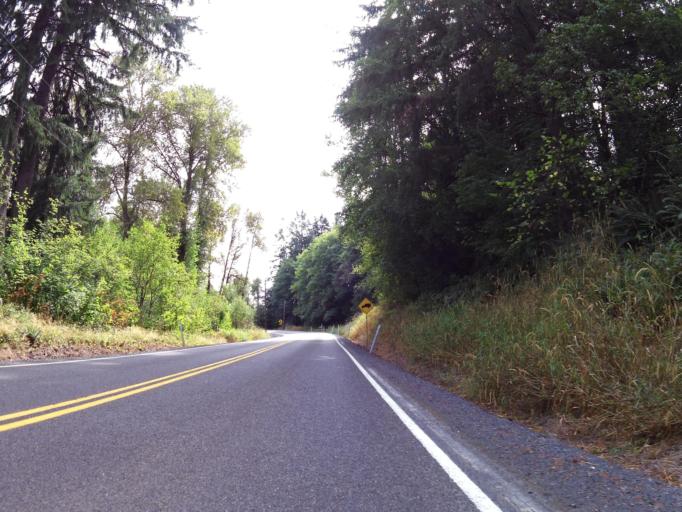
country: US
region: Washington
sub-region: Lewis County
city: Napavine
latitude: 46.5449
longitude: -122.9528
